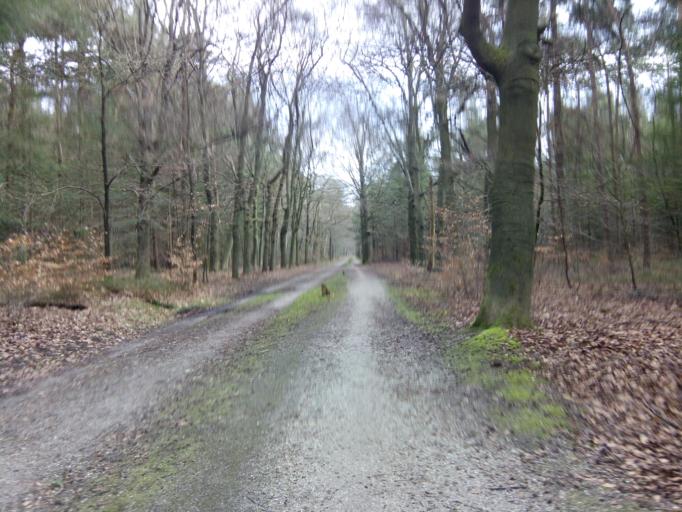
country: NL
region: Utrecht
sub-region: Gemeente Utrechtse Heuvelrug
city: Driebergen-Rijsenburg
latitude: 52.0936
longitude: 5.3169
